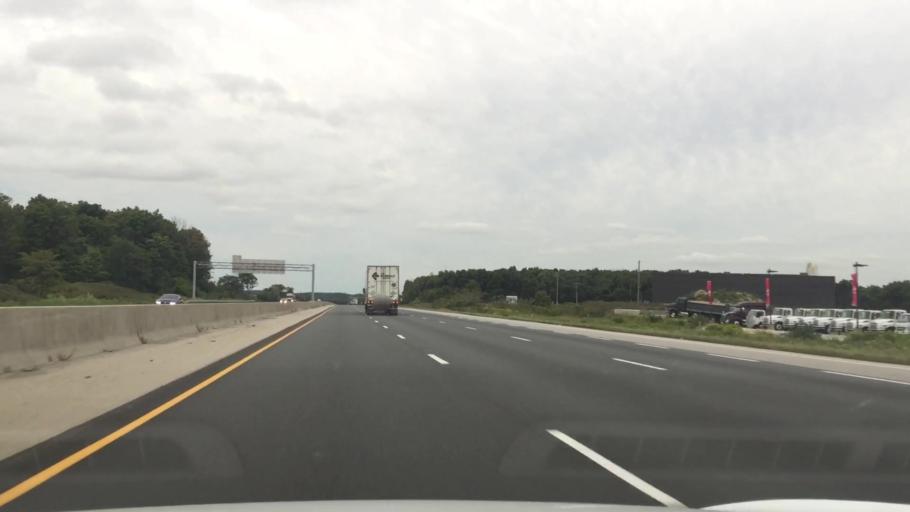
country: CA
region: Ontario
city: Kitchener
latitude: 43.3257
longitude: -80.4556
